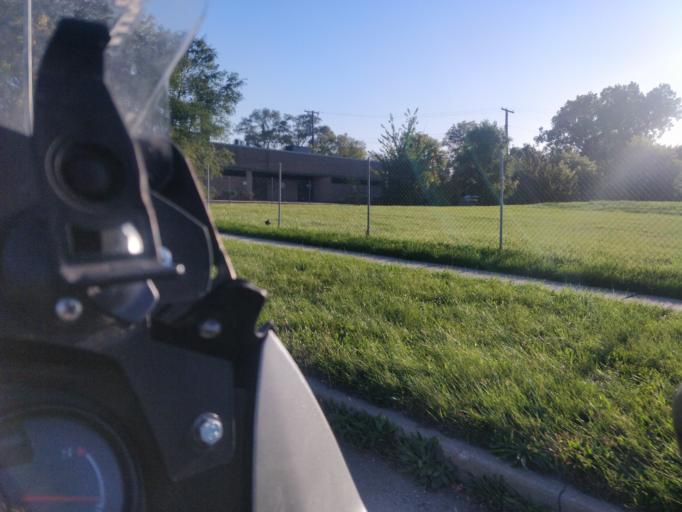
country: US
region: Michigan
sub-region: Wayne County
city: Lincoln Park
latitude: 42.2634
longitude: -83.1679
